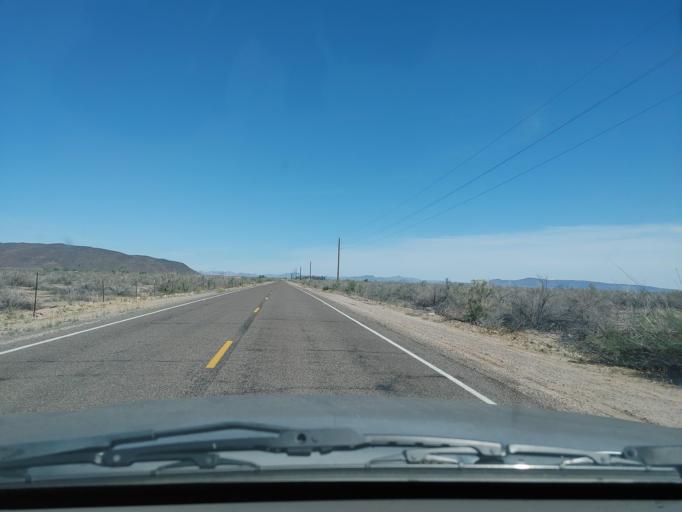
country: US
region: Arizona
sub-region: Maricopa County
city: Gila Bend
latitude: 32.9658
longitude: -113.3059
